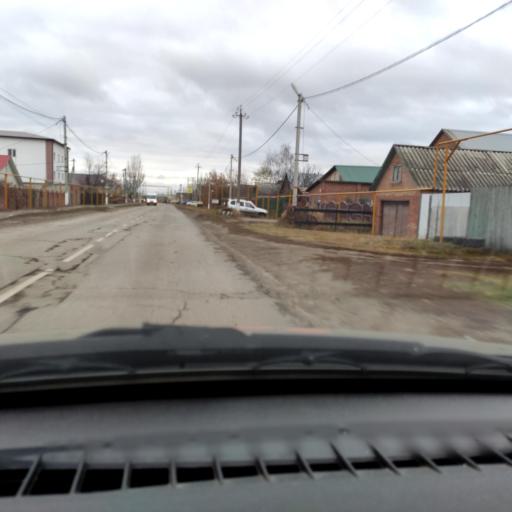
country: RU
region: Samara
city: Podstepki
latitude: 53.5164
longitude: 49.1201
